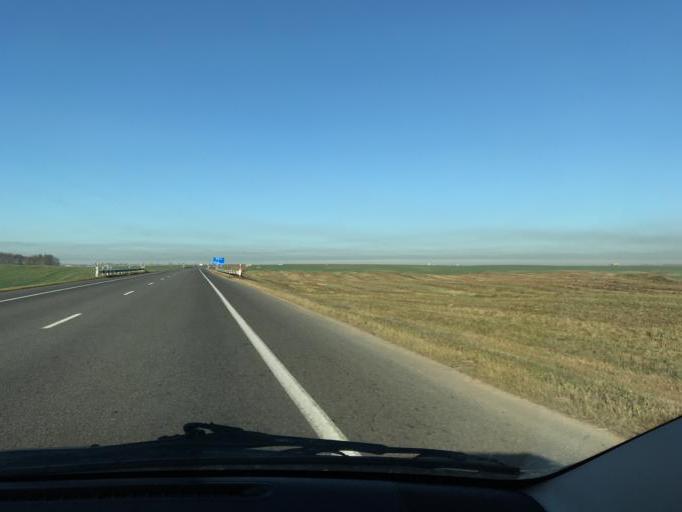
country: BY
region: Vitebsk
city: Vitebsk
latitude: 55.1052
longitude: 30.1180
